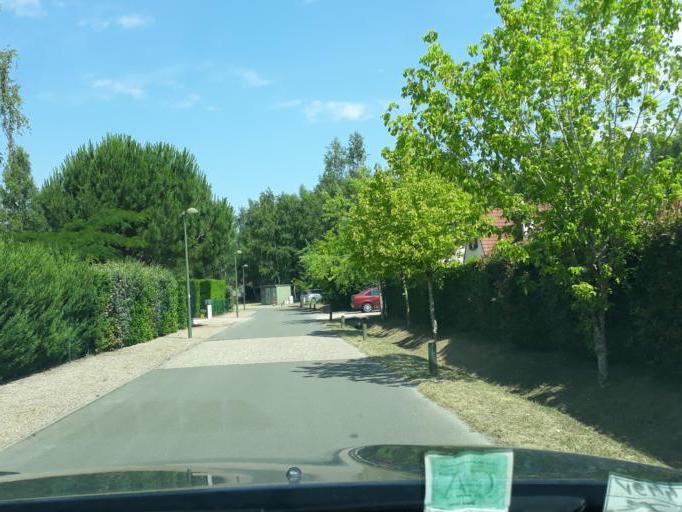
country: FR
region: Centre
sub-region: Departement du Loir-et-Cher
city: Vouzon
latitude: 47.6476
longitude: 2.0490
